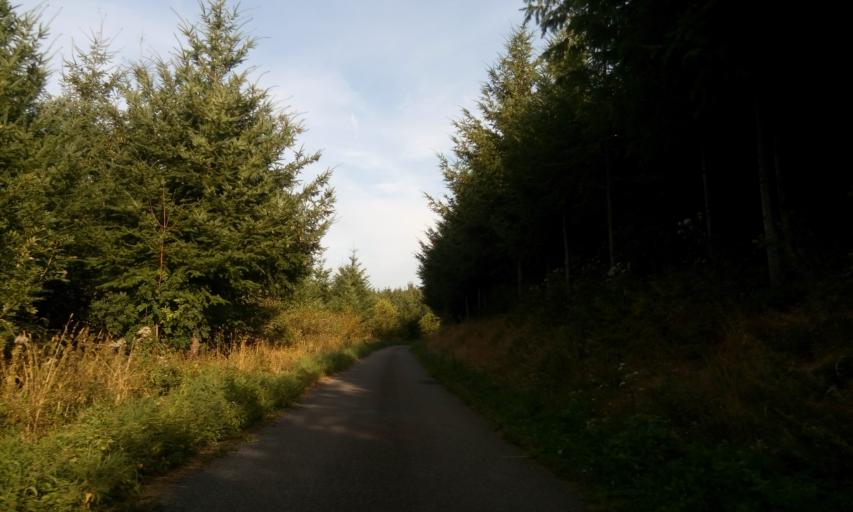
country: FR
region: Rhone-Alpes
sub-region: Departement du Rhone
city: Grandris
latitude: 45.9851
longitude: 4.4610
